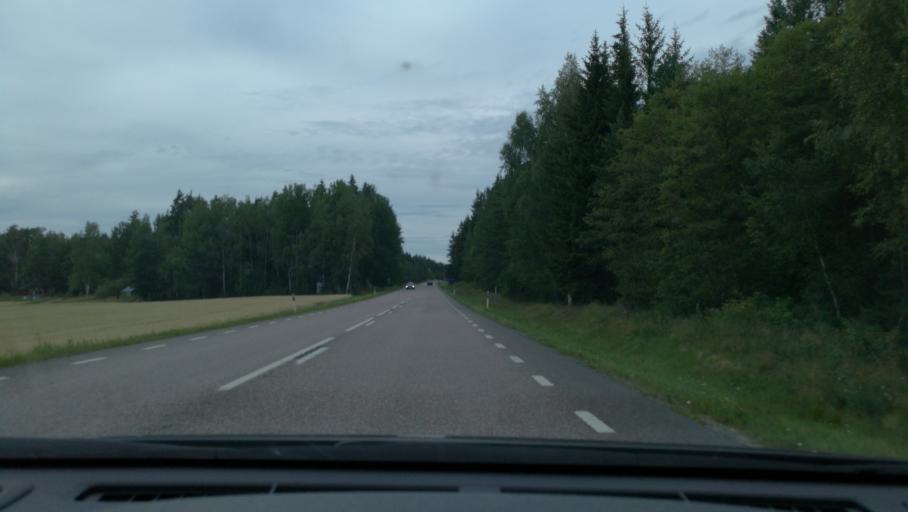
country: SE
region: Soedermanland
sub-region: Katrineholms Kommun
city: Katrineholm
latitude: 59.0332
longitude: 16.2149
